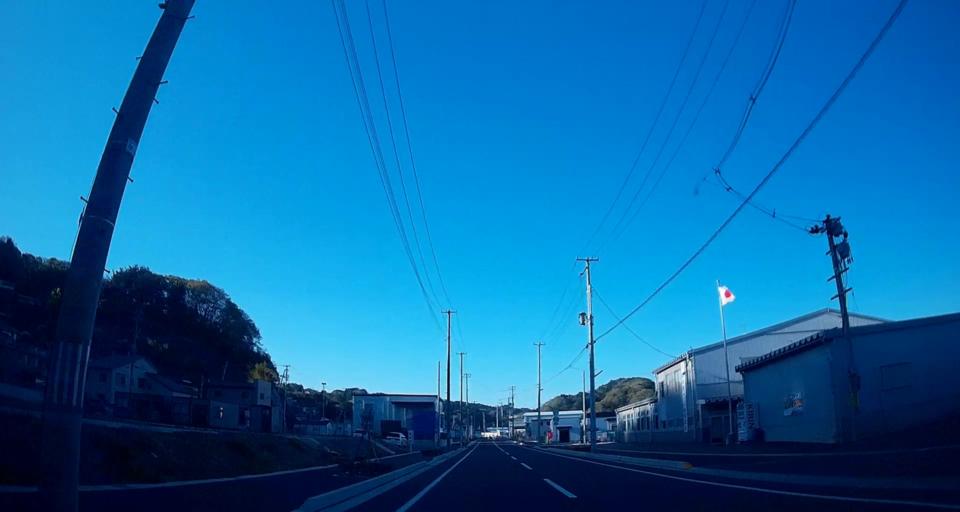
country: JP
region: Iwate
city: Miyako
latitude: 39.6419
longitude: 141.9673
